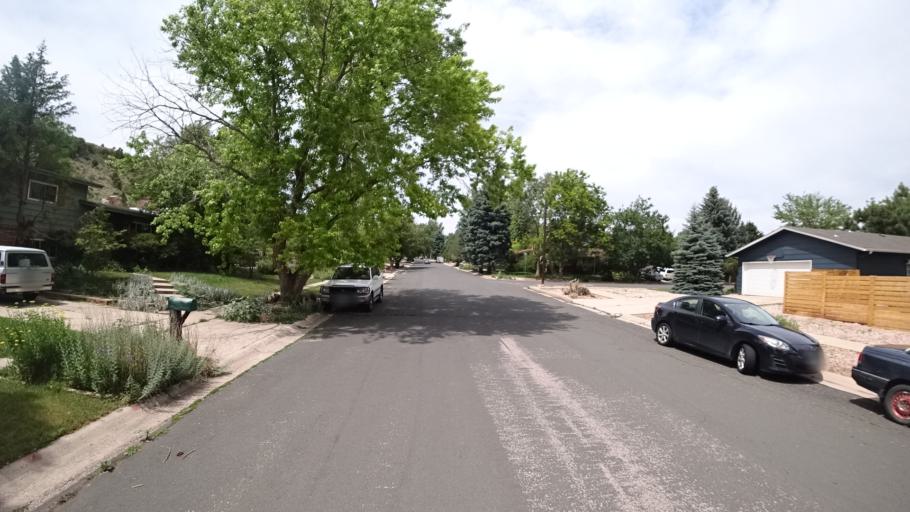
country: US
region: Colorado
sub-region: El Paso County
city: Manitou Springs
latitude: 38.8680
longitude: -104.8726
